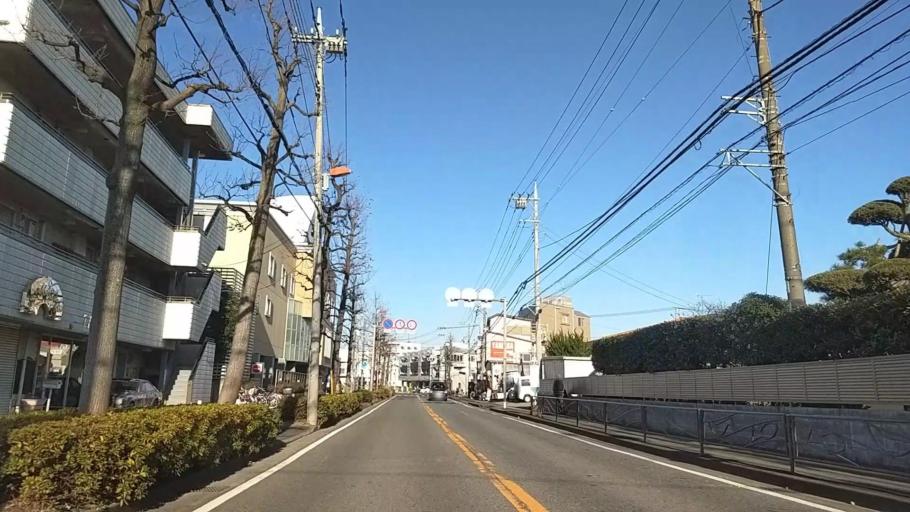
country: JP
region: Kanagawa
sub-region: Kawasaki-shi
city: Kawasaki
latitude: 35.5889
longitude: 139.6402
